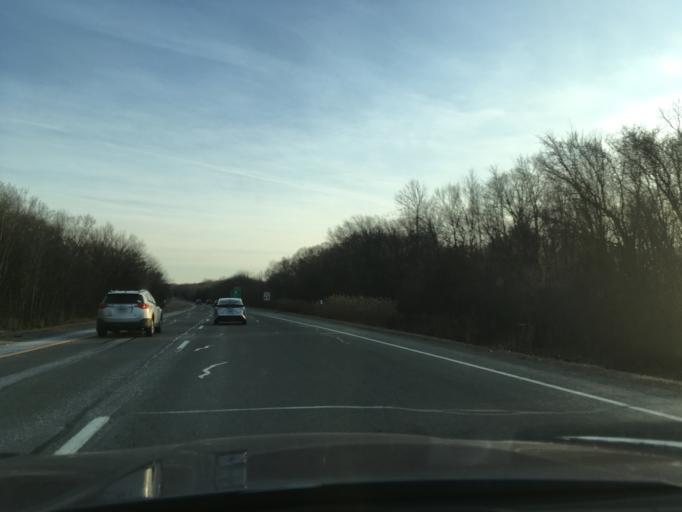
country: US
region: Rhode Island
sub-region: Providence County
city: Johnston
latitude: 41.8003
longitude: -71.5108
